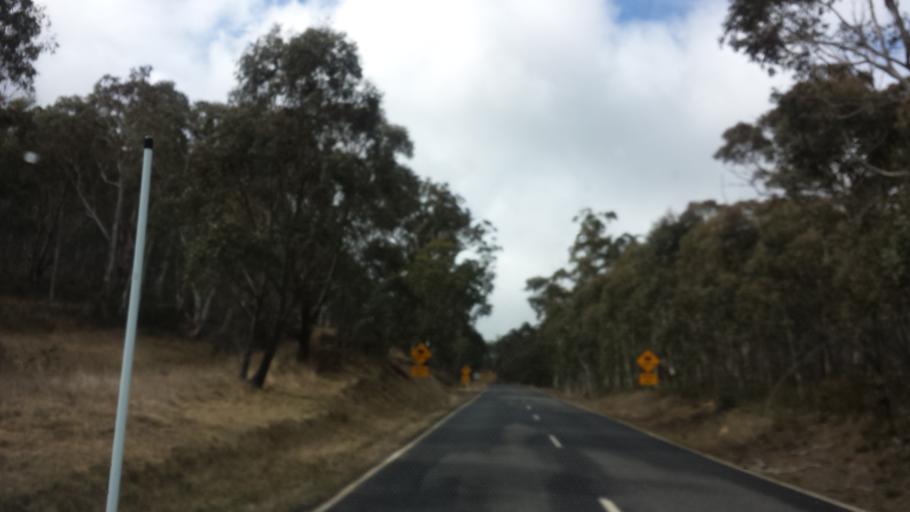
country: AU
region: Victoria
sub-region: Alpine
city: Mount Beauty
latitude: -37.1350
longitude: 147.4887
